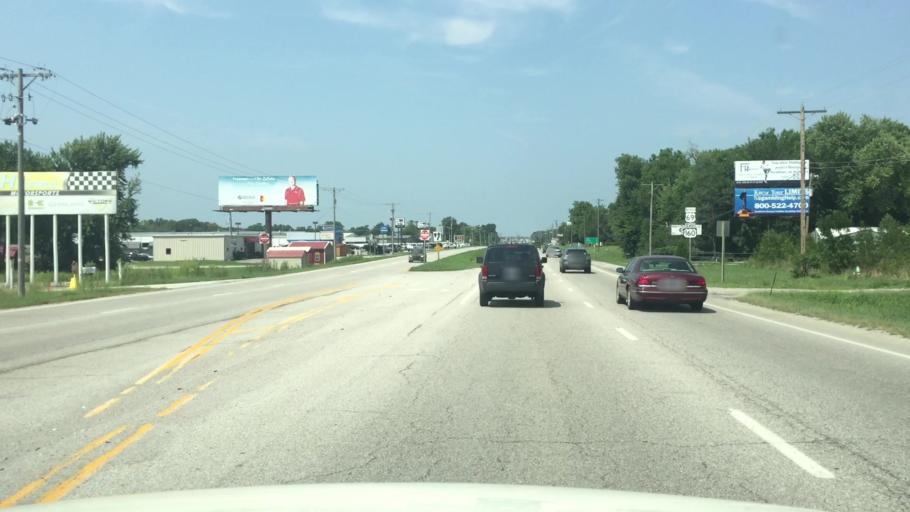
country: US
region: Kansas
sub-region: Crawford County
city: Frontenac
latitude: 37.4561
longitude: -94.7051
